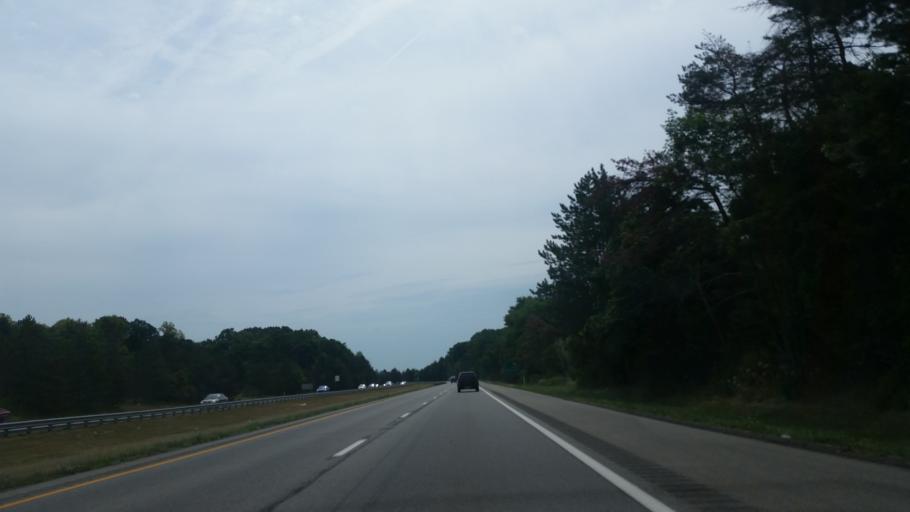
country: US
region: Ohio
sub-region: Cuyahoga County
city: Solon
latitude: 41.3975
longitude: -81.4523
